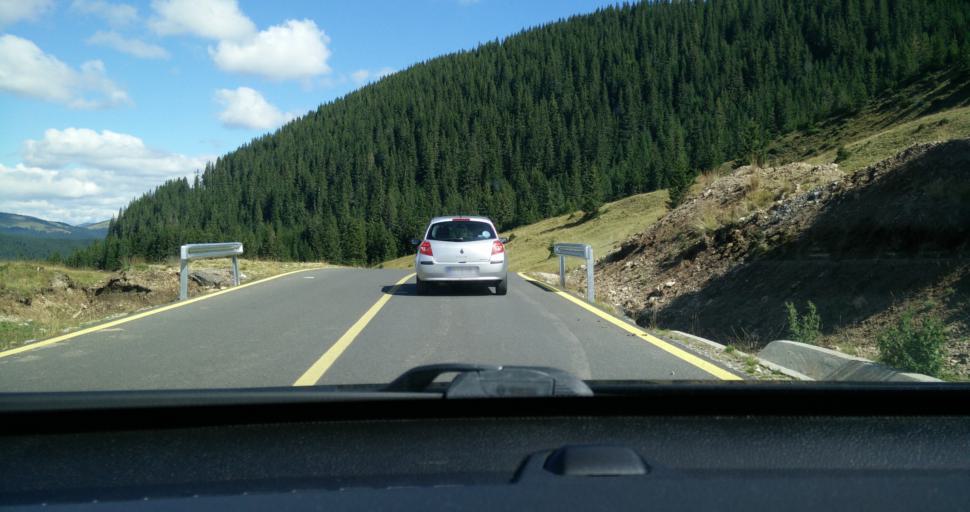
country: RO
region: Gorj
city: Novaci-Straini
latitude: 45.3894
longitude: 23.6440
